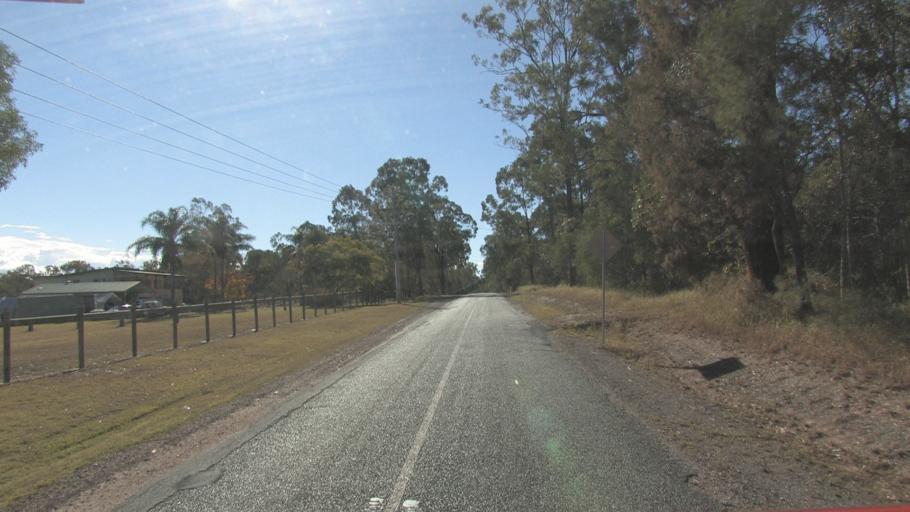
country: AU
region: Queensland
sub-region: Logan
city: Chambers Flat
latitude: -27.7963
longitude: 153.0705
